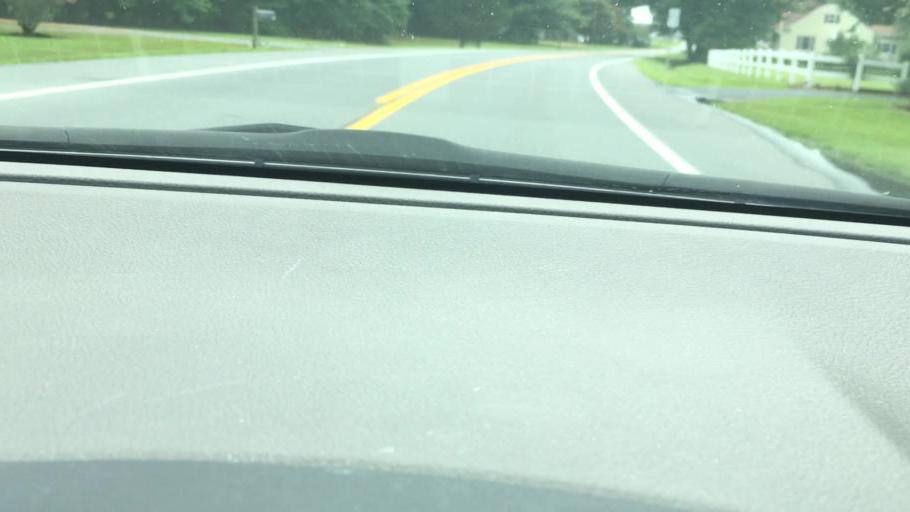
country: US
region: Maryland
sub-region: Worcester County
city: Pocomoke City
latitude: 38.0629
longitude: -75.5410
